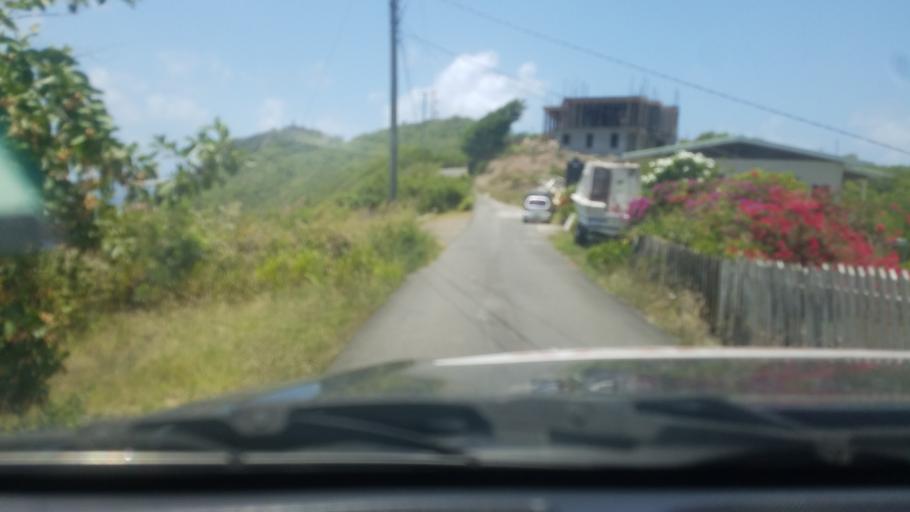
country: LC
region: Vieux-Fort
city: Vieux Fort
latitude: 13.7165
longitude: -60.9478
